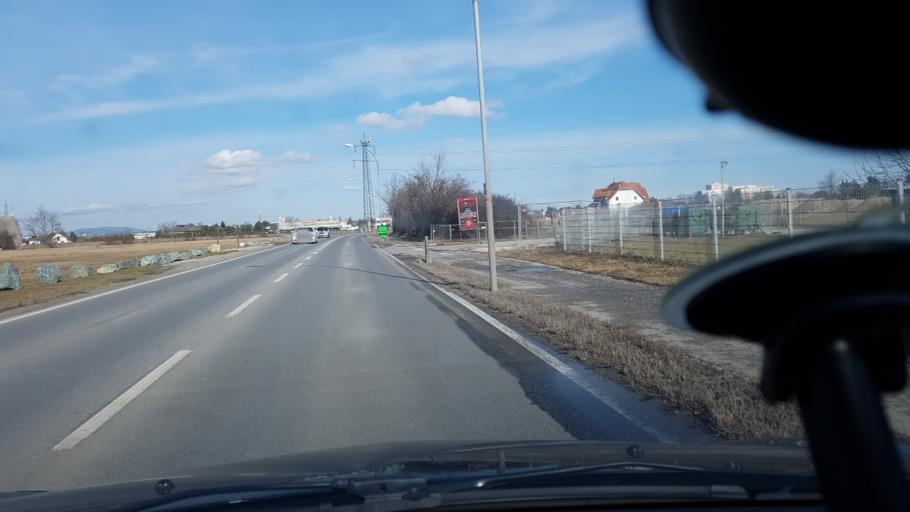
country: AT
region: Lower Austria
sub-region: Wiener Neustadt Stadt
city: Wiener Neustadt
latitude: 47.8075
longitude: 16.2125
